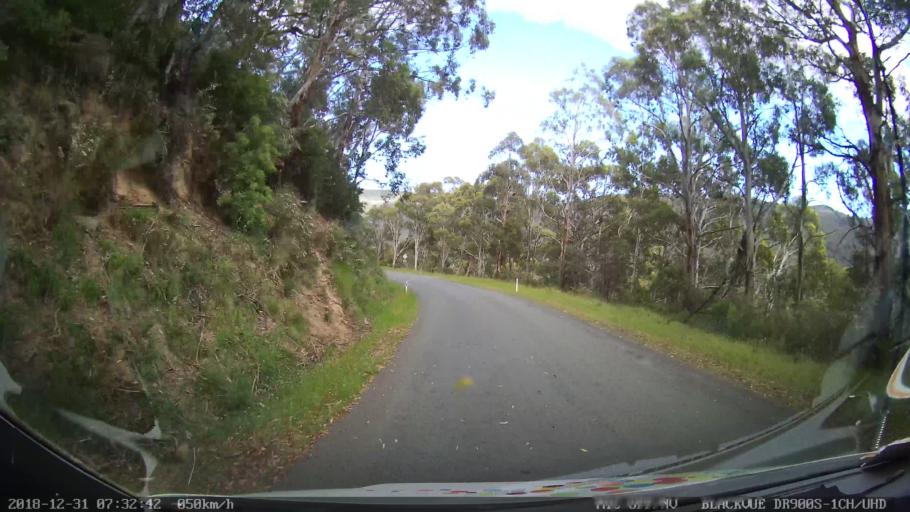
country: AU
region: New South Wales
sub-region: Snowy River
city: Jindabyne
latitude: -36.3301
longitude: 148.4631
